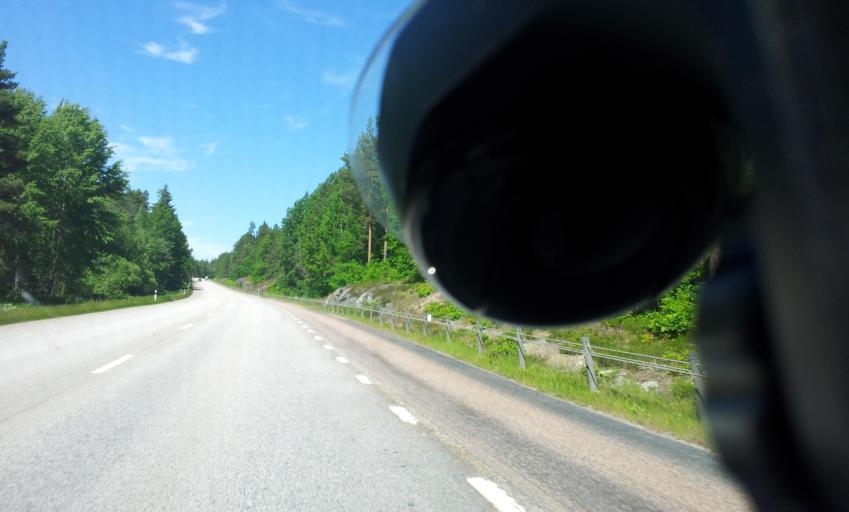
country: SE
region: Kalmar
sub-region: Vasterviks Kommun
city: Ankarsrum
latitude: 57.6185
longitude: 16.4681
